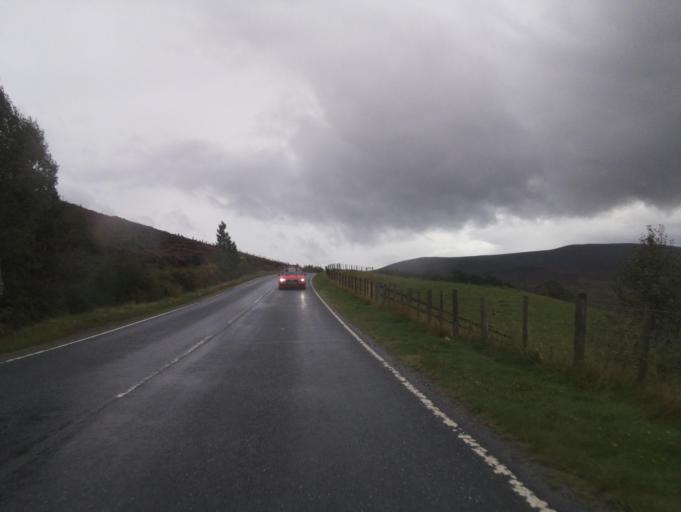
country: GB
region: Scotland
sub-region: Highland
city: Grantown on Spey
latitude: 57.2764
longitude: -3.5536
